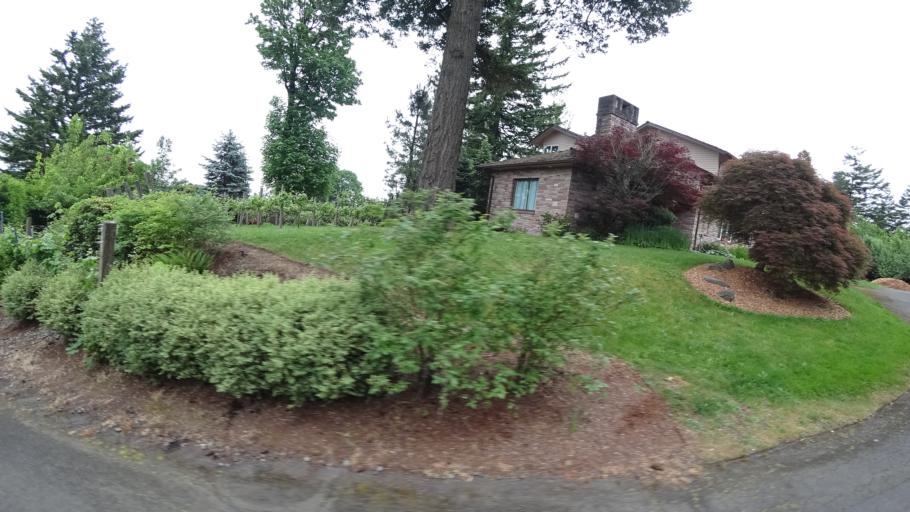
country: US
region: Oregon
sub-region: Multnomah County
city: Portland
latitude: 45.4861
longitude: -122.6921
